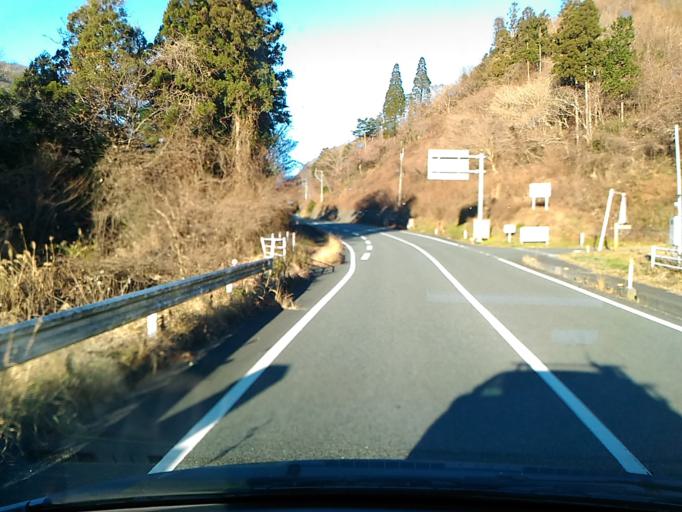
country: JP
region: Ibaraki
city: Kitaibaraki
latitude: 36.9338
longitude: 140.6841
